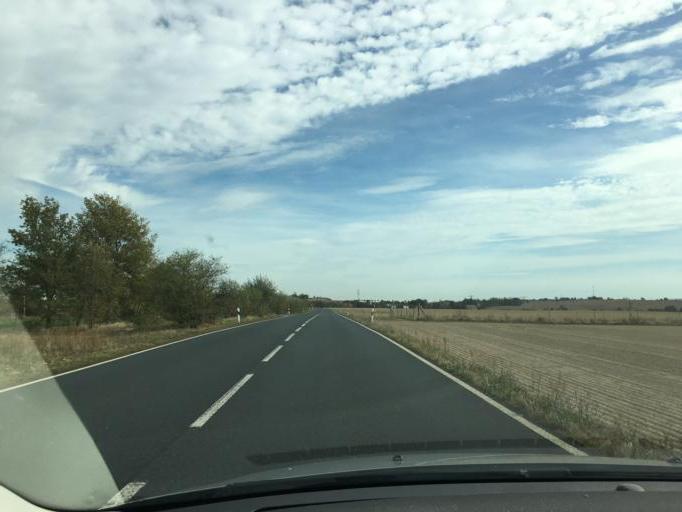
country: DE
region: Saxony
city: Lommatzsch
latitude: 51.2262
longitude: 13.3471
